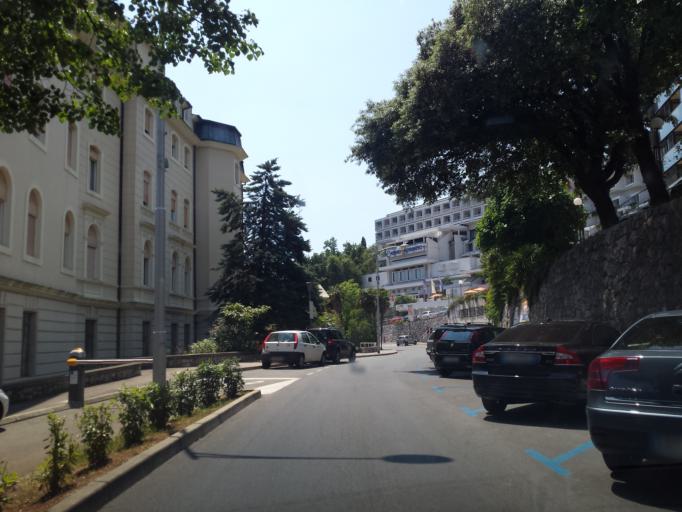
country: HR
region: Primorsko-Goranska
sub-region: Grad Opatija
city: Opatija
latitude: 45.3267
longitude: 14.2995
